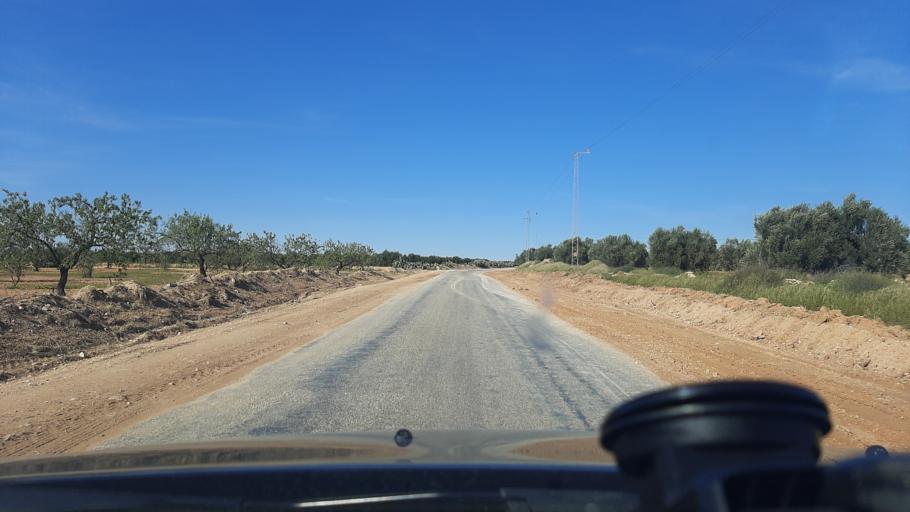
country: TN
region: Safaqis
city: Sfax
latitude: 34.9305
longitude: 10.5699
